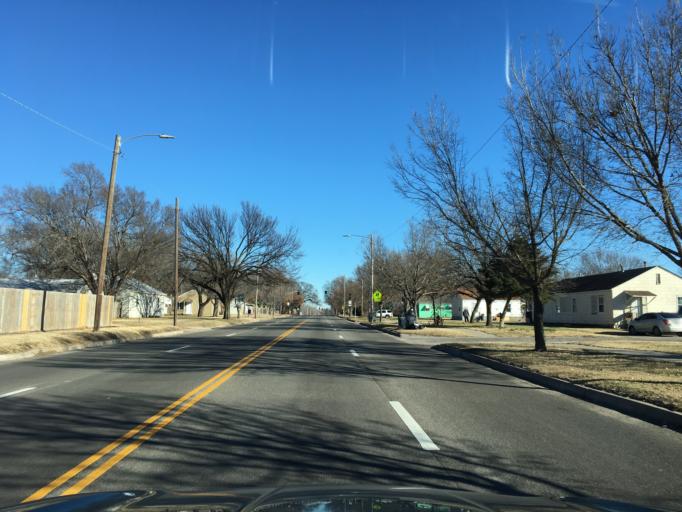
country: US
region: Kansas
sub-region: Sedgwick County
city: Wichita
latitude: 37.6719
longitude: -97.2852
